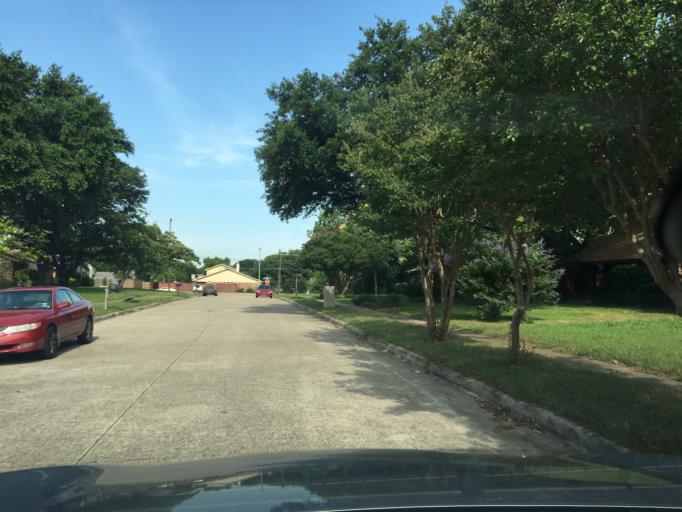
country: US
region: Texas
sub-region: Dallas County
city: Richardson
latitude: 32.9660
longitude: -96.6814
